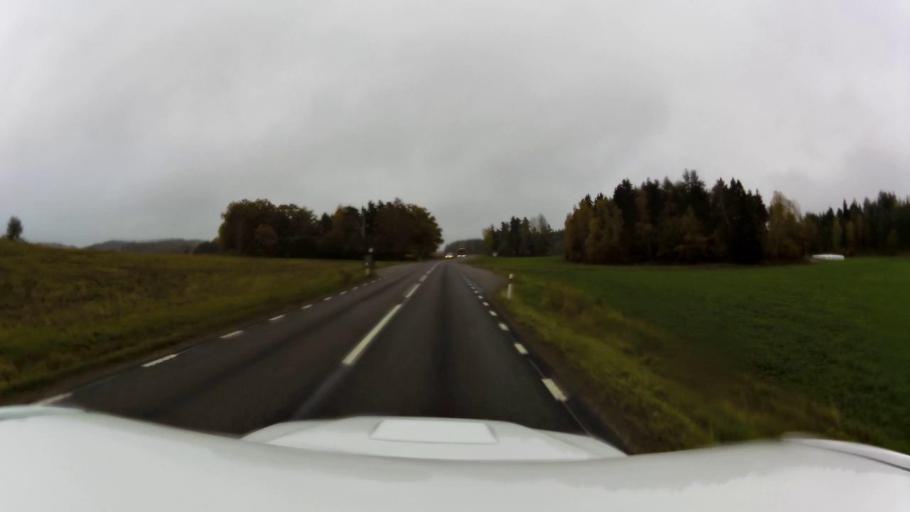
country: SE
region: OEstergoetland
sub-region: Linkopings Kommun
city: Linghem
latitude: 58.3691
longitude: 15.8185
